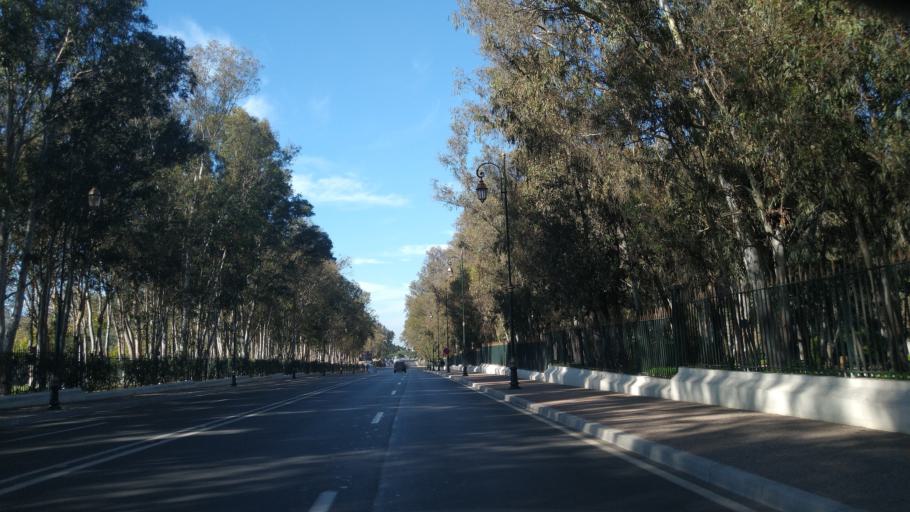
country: MA
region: Rabat-Sale-Zemmour-Zaer
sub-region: Rabat
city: Rabat
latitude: 33.9829
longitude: -6.8465
